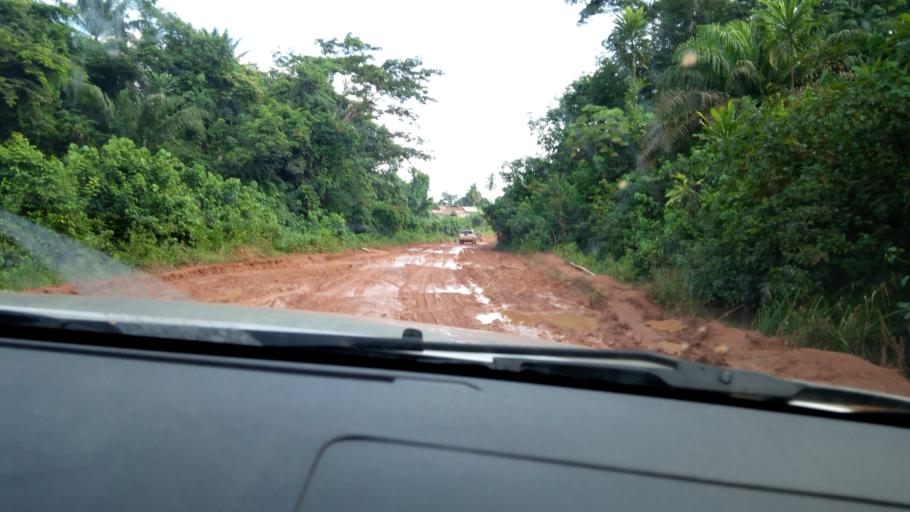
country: CI
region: Dix-Huit Montagnes
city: Toulepleu Guere
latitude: 6.5265
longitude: -8.8421
